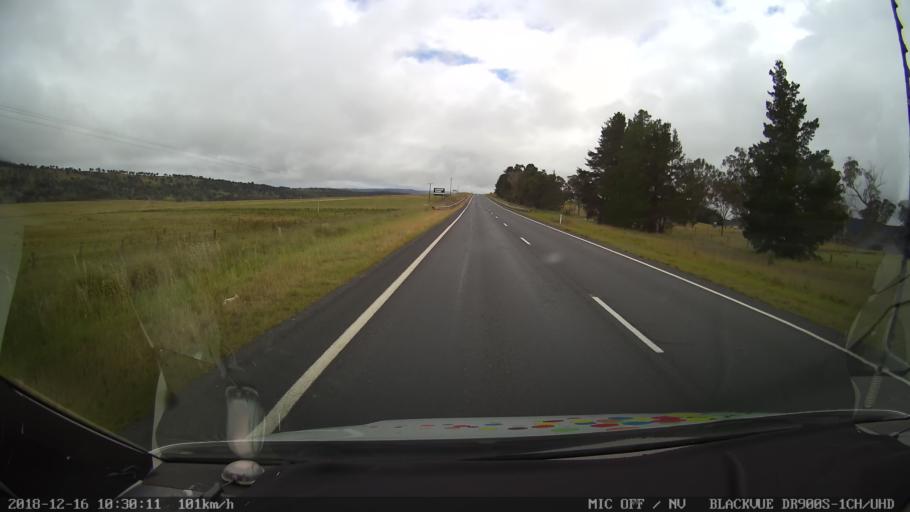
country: AU
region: New South Wales
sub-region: Tenterfield Municipality
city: Carrolls Creek
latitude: -29.0969
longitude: 152.0019
